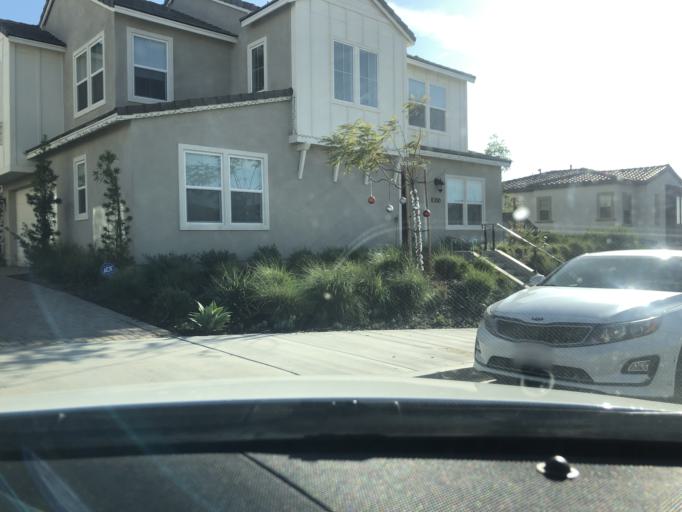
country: US
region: California
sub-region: San Diego County
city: Bonita
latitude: 32.5989
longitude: -117.0021
